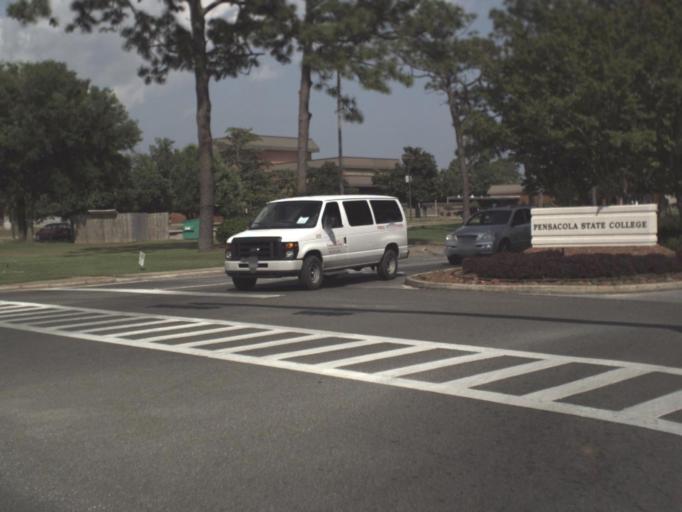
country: US
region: Florida
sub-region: Escambia County
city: Ferry Pass
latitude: 30.4809
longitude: -87.2054
